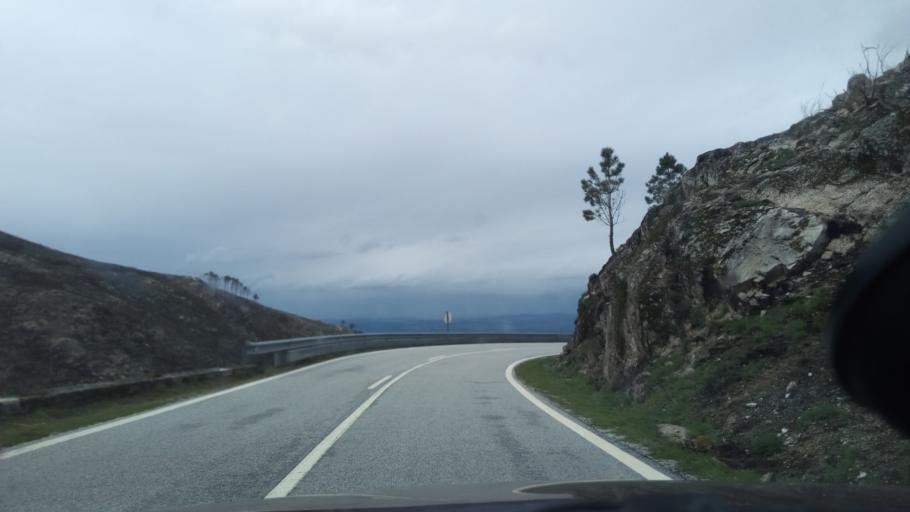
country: PT
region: Guarda
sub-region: Manteigas
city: Manteigas
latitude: 40.4543
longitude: -7.5860
